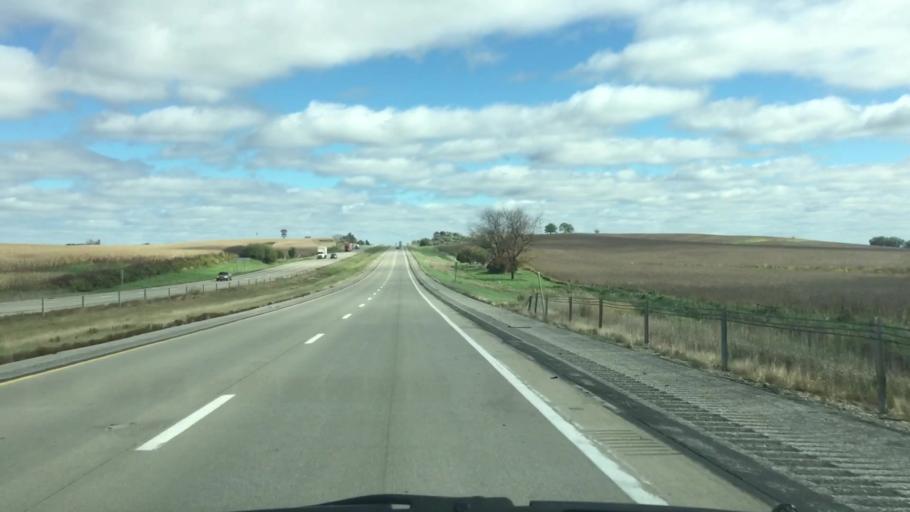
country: US
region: Iowa
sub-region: Iowa County
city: Williamsburg
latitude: 41.6903
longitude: -92.0847
